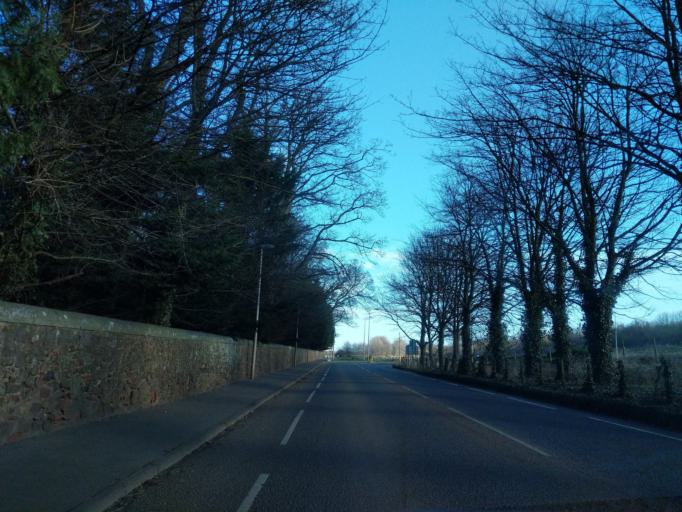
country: GB
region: Scotland
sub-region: East Lothian
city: East Linton
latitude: 55.9856
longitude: -2.6471
